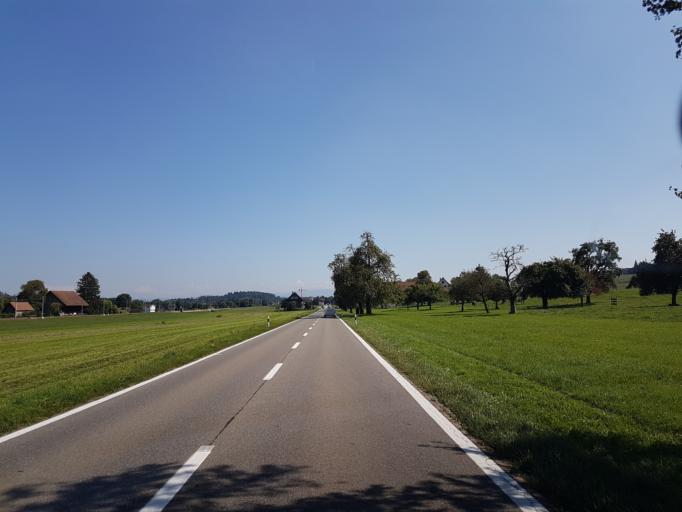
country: CH
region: Aargau
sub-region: Bezirk Muri
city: Muri
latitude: 47.2860
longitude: 8.3276
